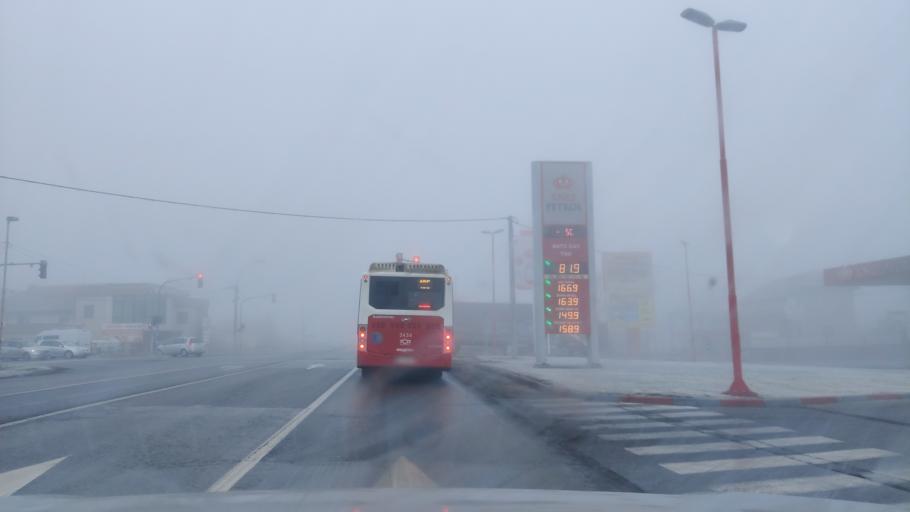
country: RS
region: Central Serbia
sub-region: Belgrade
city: Stari Grad
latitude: 44.8507
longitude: 20.4855
